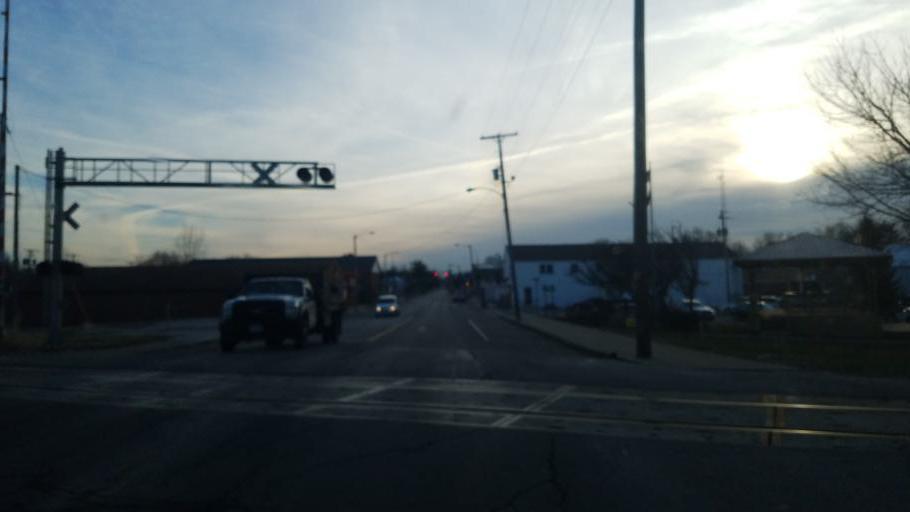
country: US
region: Ohio
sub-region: Morrow County
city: Cardington
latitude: 40.5004
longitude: -82.8962
